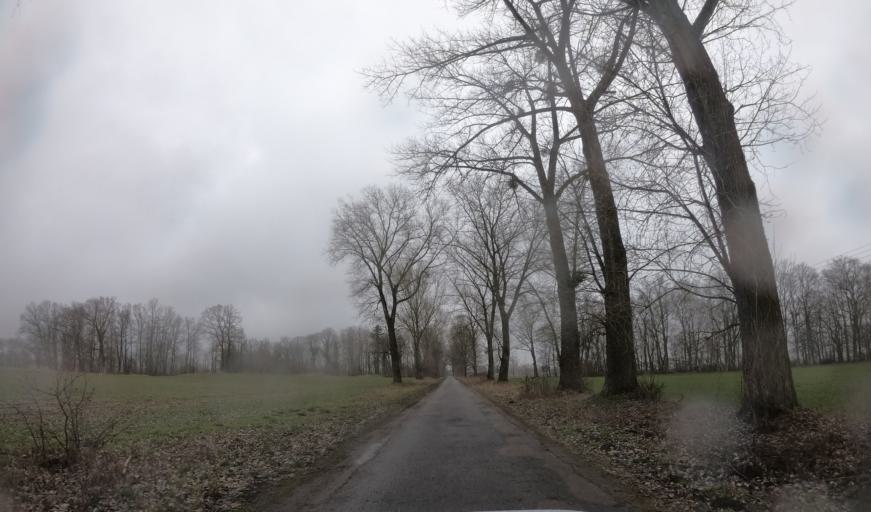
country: PL
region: West Pomeranian Voivodeship
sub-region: Powiat kamienski
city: Kamien Pomorski
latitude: 53.9058
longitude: 14.8316
